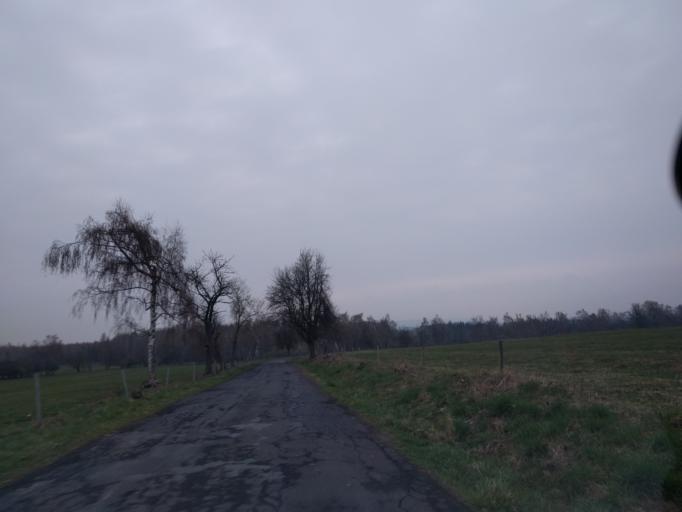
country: CZ
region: Karlovarsky
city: Bochov
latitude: 50.1245
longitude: 13.0846
